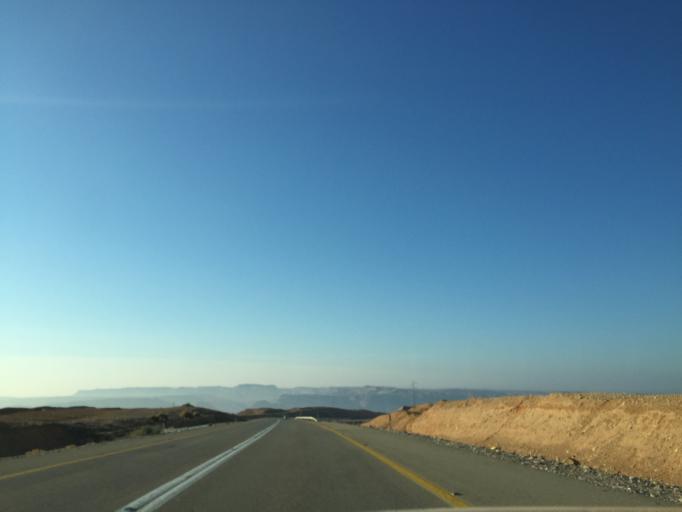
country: IL
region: Southern District
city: Mitzpe Ramon
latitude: 30.3568
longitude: 34.9612
